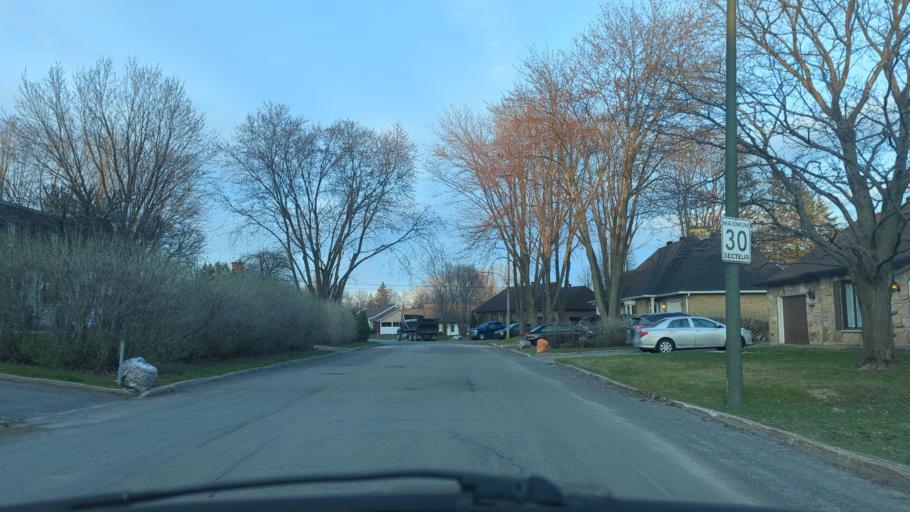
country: CA
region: Quebec
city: Quebec
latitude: 46.8514
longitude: -71.2623
